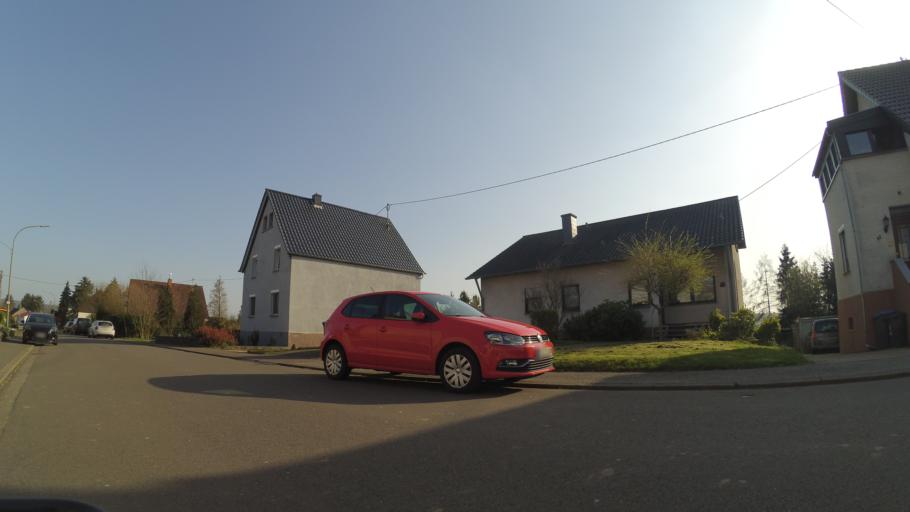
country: DE
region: Saarland
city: Heusweiler
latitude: 49.3421
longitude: 6.9145
